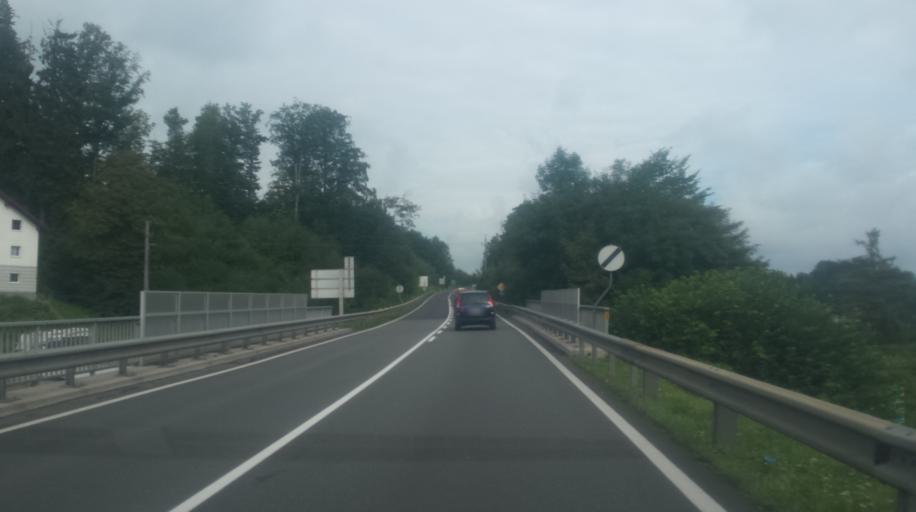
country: AT
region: Upper Austria
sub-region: Politischer Bezirk Gmunden
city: Altmunster
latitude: 47.9502
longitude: 13.7504
